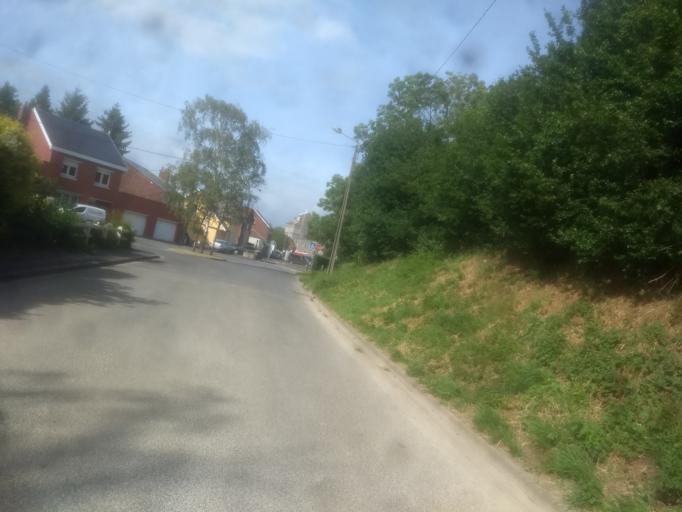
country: FR
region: Nord-Pas-de-Calais
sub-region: Departement du Pas-de-Calais
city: Feuchy
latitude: 50.2955
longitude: 2.8368
